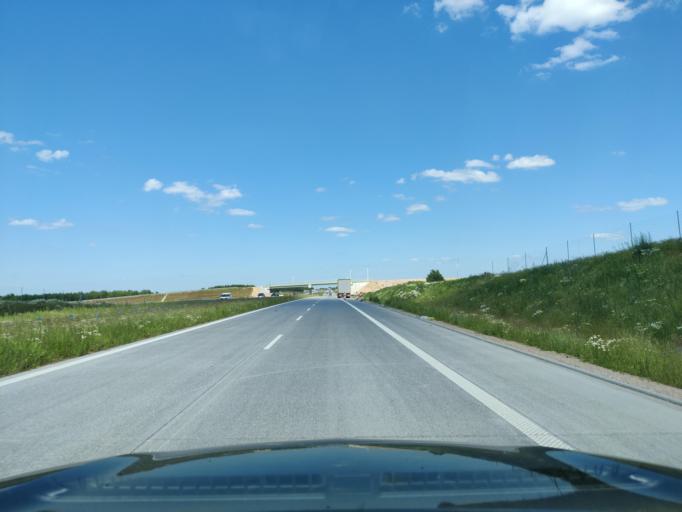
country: PL
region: Masovian Voivodeship
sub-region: Powiat mlawski
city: Wisniewo
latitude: 53.0242
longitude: 20.3447
